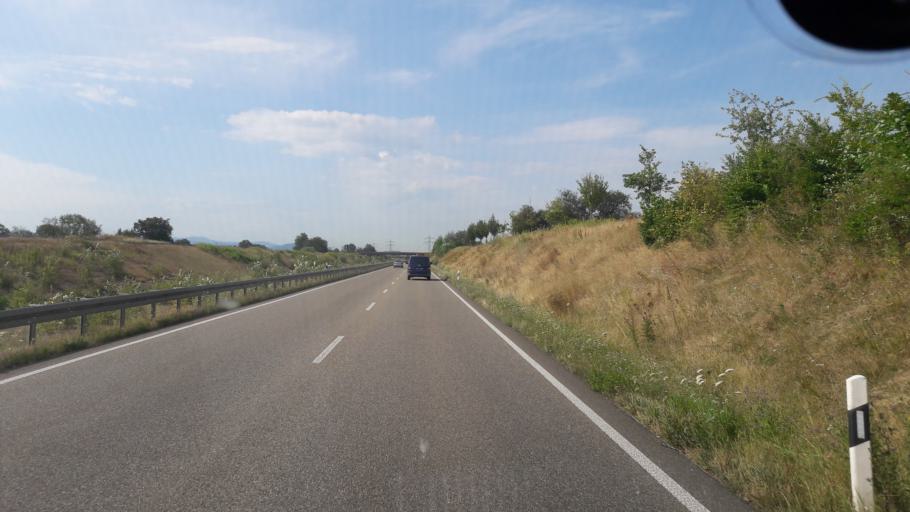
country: DE
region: Baden-Wuerttemberg
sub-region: Karlsruhe Region
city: Durmersheim
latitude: 48.9168
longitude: 8.2690
